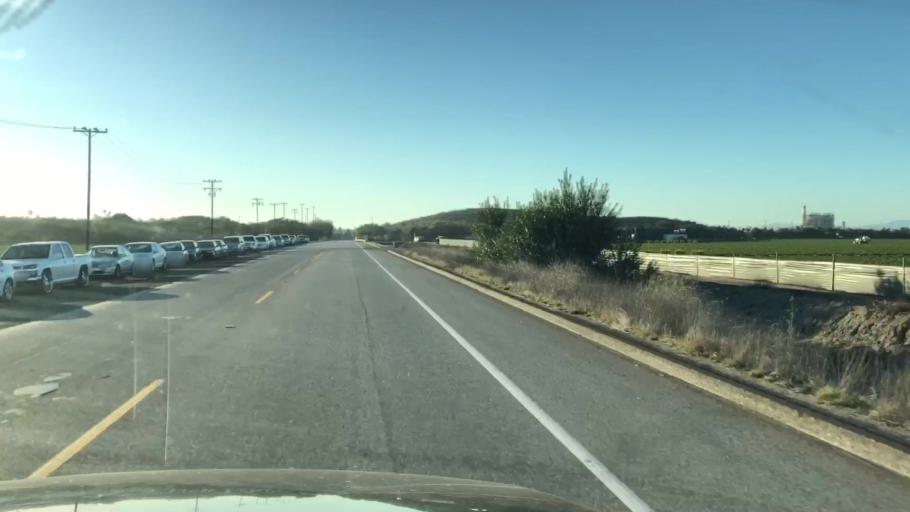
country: US
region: California
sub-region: Ventura County
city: Oxnard Shores
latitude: 34.1978
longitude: -119.2333
